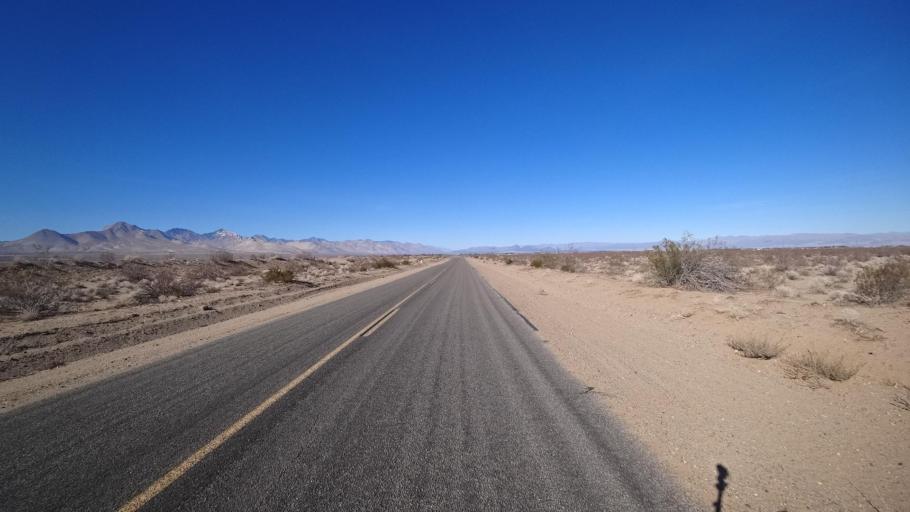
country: US
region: California
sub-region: Kern County
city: Inyokern
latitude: 35.5961
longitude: -117.7964
